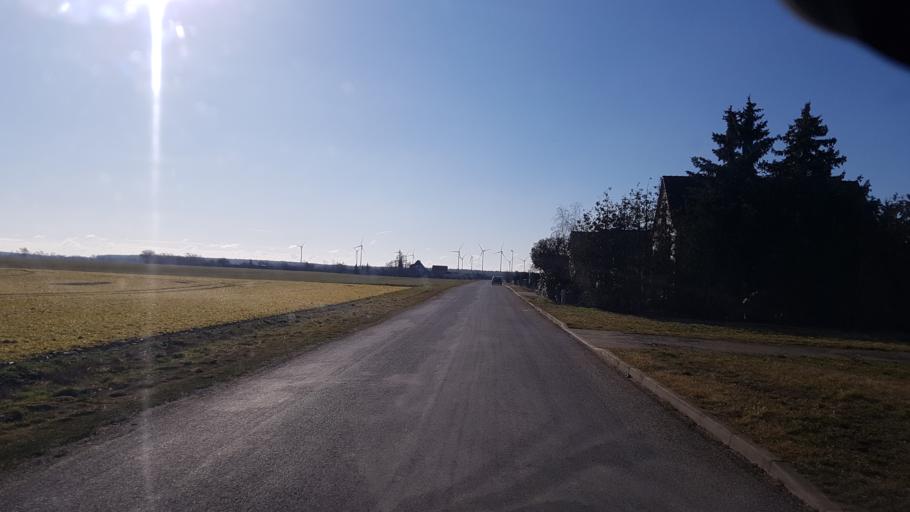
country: DE
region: Brandenburg
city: Muhlberg
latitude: 51.5020
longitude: 13.2322
